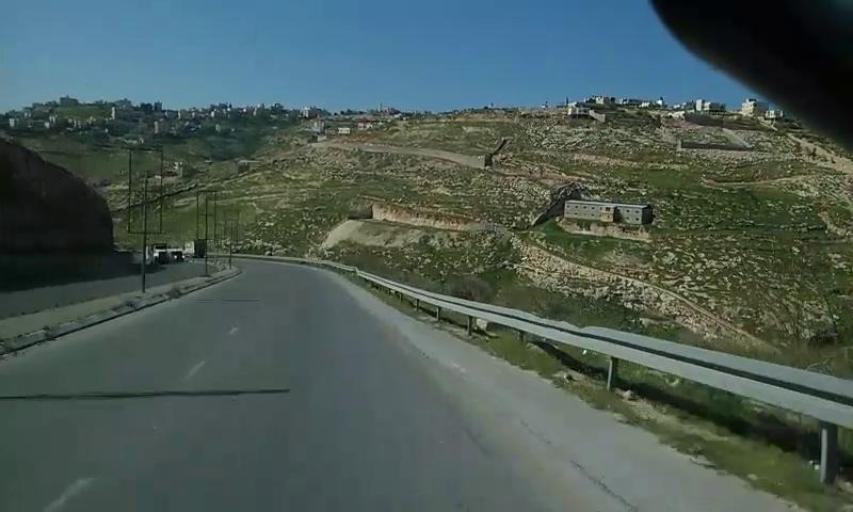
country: PS
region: West Bank
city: Abu Dis
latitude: 31.7499
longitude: 35.2780
